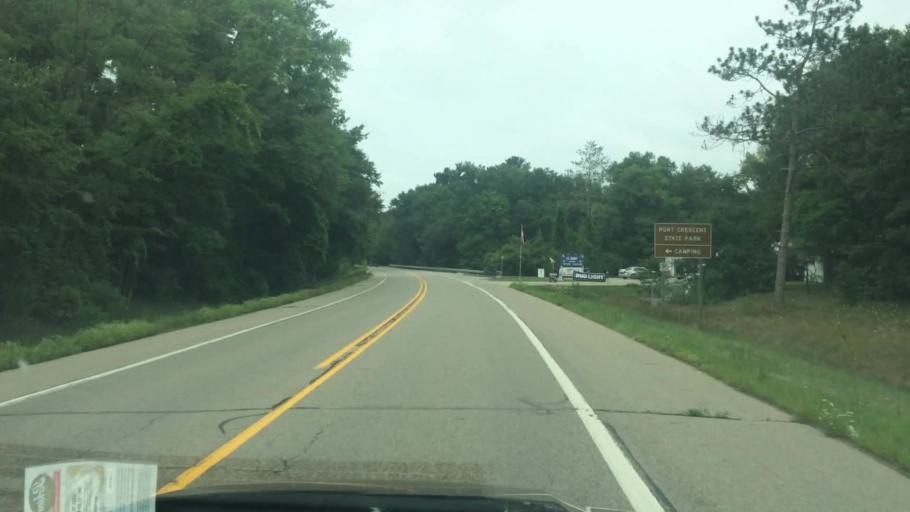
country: US
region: Michigan
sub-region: Huron County
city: Bad Axe
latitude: 44.0048
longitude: -83.0525
